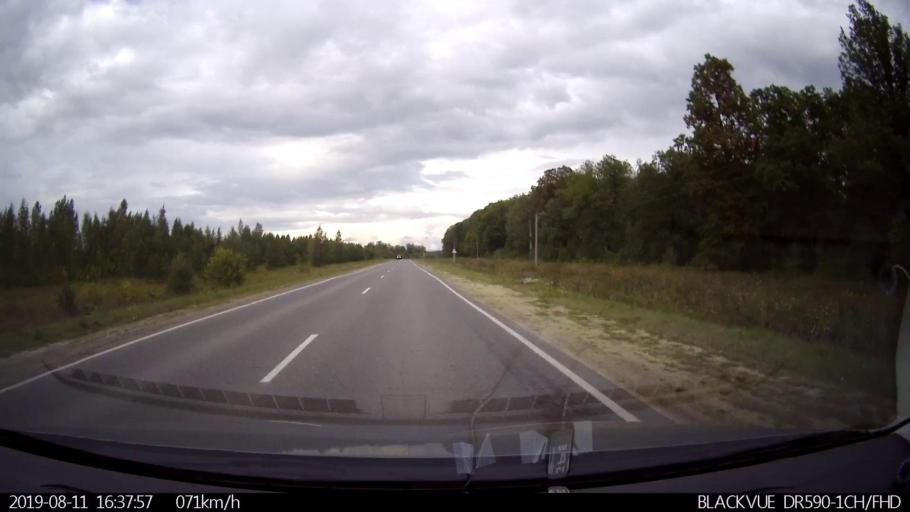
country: RU
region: Ulyanovsk
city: Mayna
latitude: 54.1314
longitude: 47.6195
